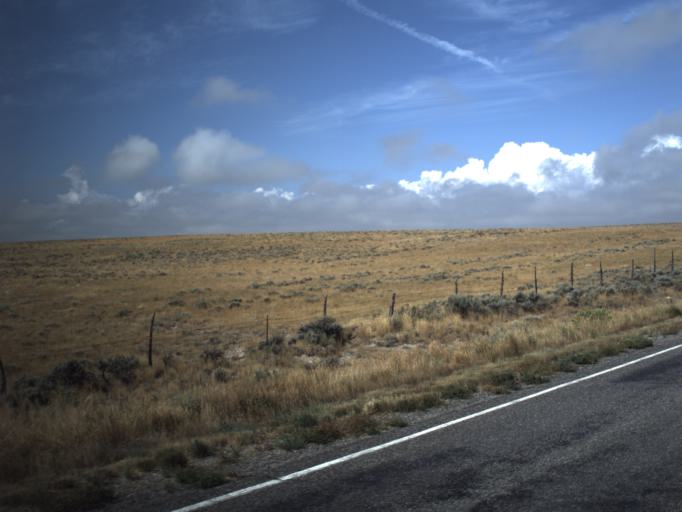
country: US
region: Wyoming
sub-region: Uinta County
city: Evanston
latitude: 41.4408
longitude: -111.0735
